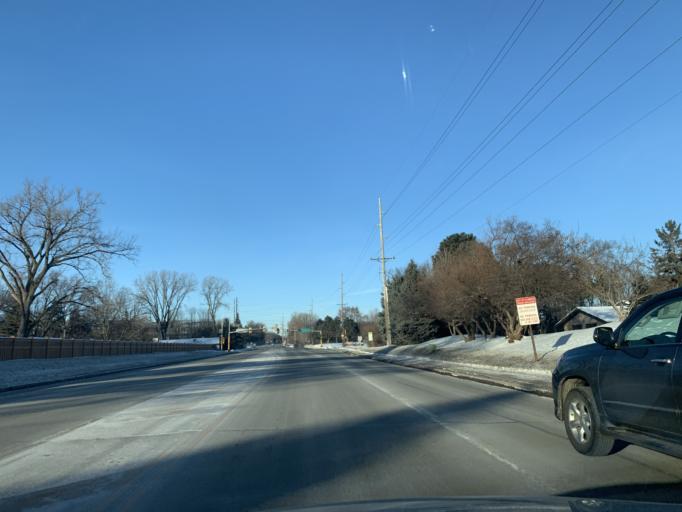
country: US
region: Minnesota
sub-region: Hennepin County
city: Wayzata
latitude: 44.9791
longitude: -93.5020
